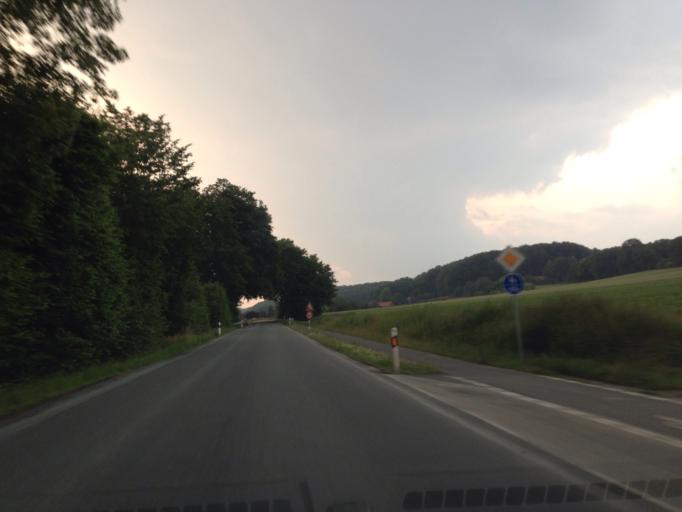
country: DE
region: North Rhine-Westphalia
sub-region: Regierungsbezirk Munster
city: Havixbeck
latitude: 51.9401
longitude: 7.4125
